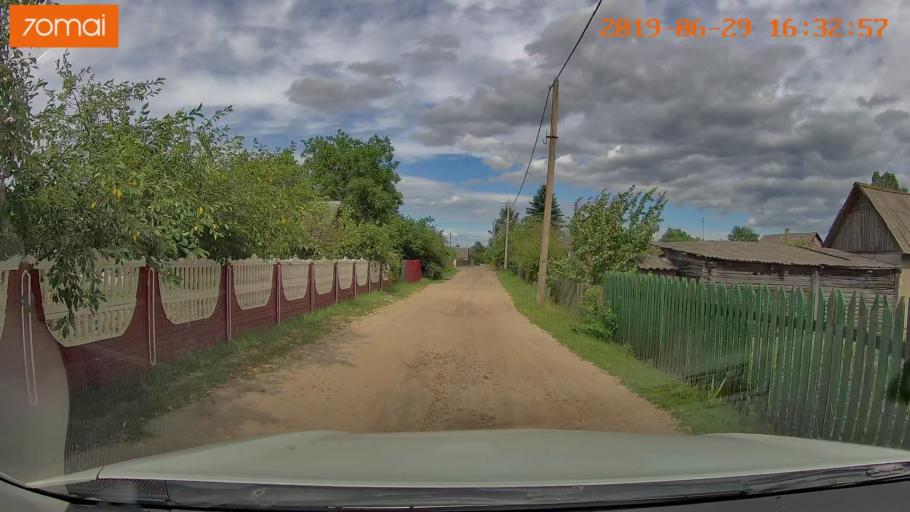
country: BY
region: Brest
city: Luninyets
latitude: 52.2016
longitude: 27.0122
